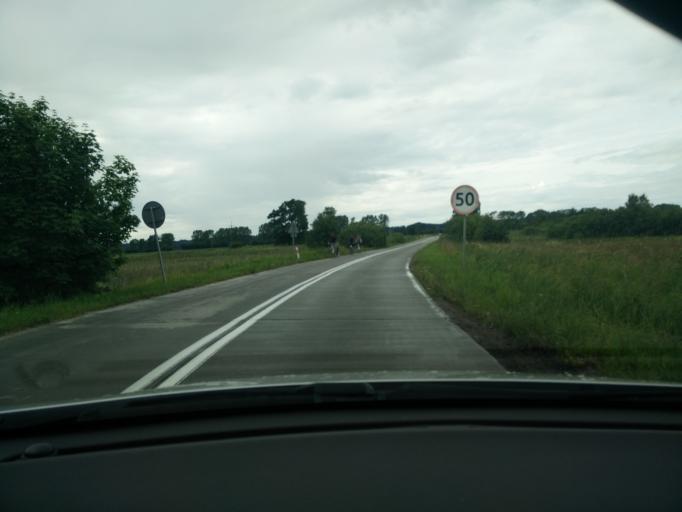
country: PL
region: Pomeranian Voivodeship
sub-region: Powiat pucki
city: Mrzezino
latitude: 54.6228
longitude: 18.4396
